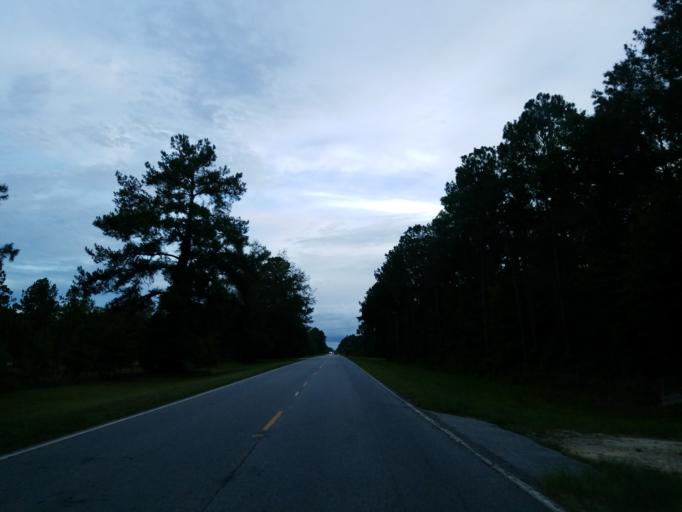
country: US
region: Georgia
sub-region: Echols County
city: Statenville
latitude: 30.6540
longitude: -83.0255
